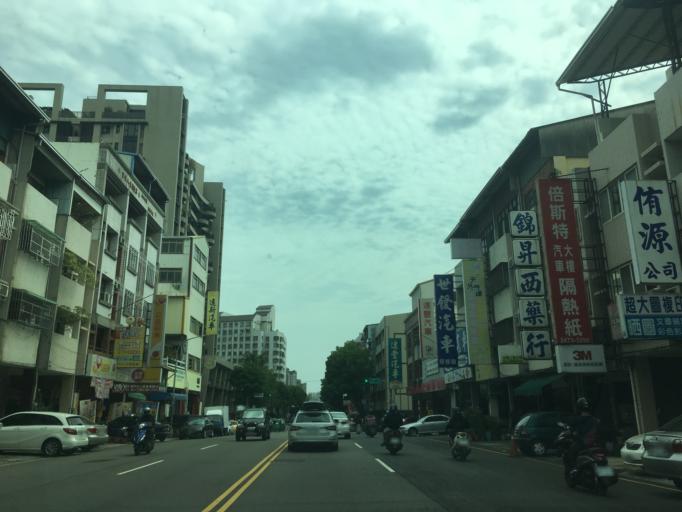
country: TW
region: Taiwan
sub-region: Taichung City
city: Taichung
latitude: 24.1387
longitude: 120.6499
